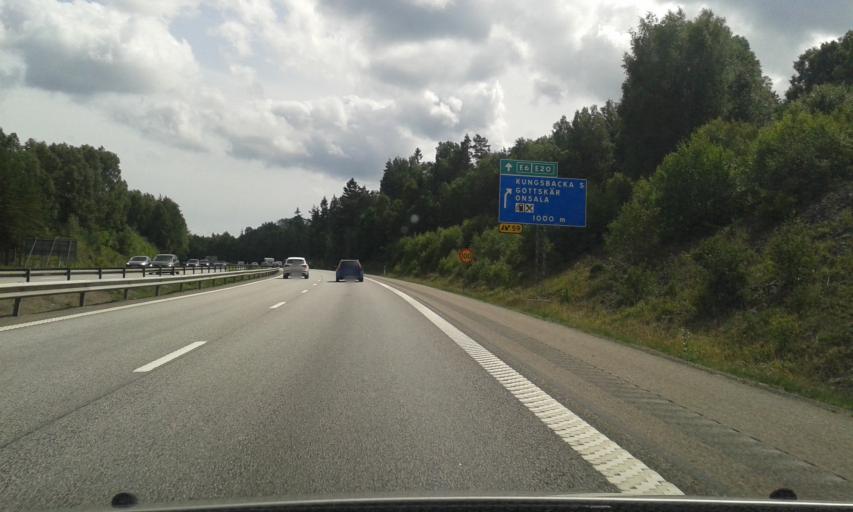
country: SE
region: Halland
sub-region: Kungsbacka Kommun
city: Kungsbacka
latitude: 57.4820
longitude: 12.0431
